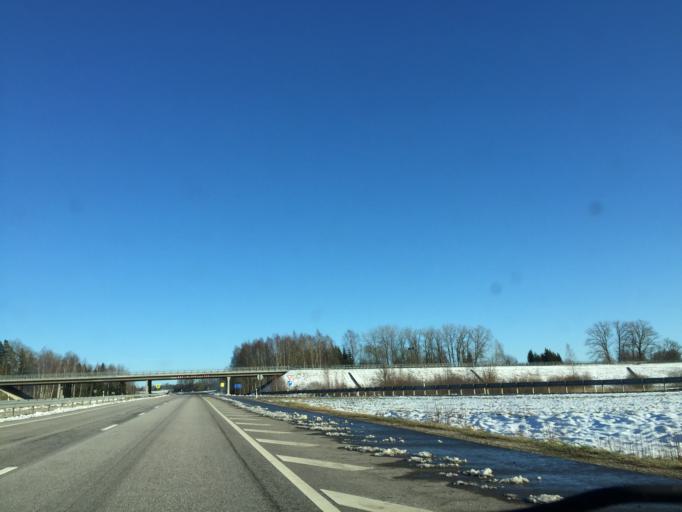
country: LV
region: Talsu Rajons
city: Talsi
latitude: 57.1958
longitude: 22.5659
